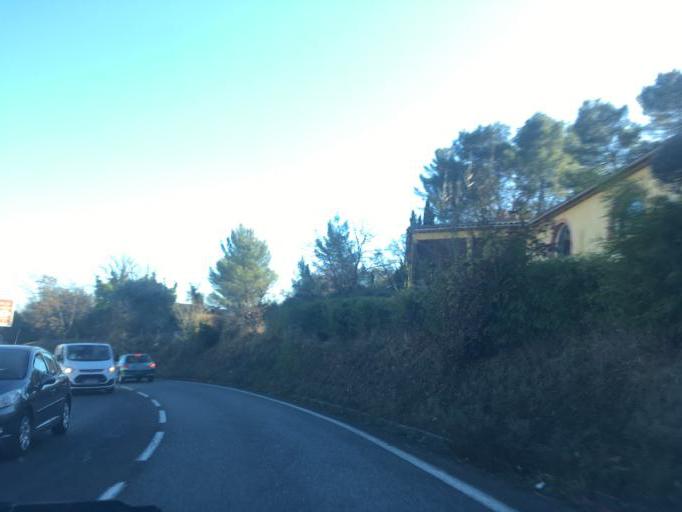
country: FR
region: Provence-Alpes-Cote d'Azur
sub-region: Departement du Var
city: Draguignan
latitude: 43.5282
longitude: 6.4402
